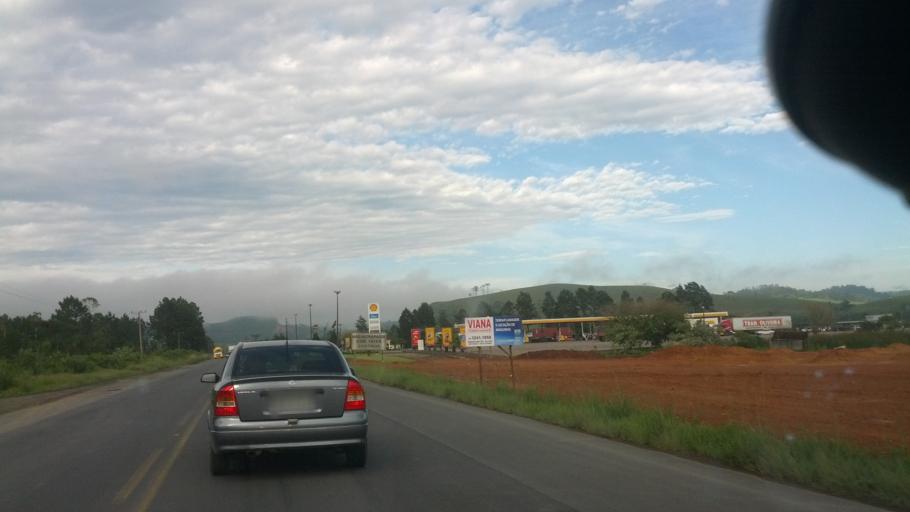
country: BR
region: Santa Catarina
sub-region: Otacilio Costa
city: Otacilio Costa
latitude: -27.2494
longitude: -49.9867
